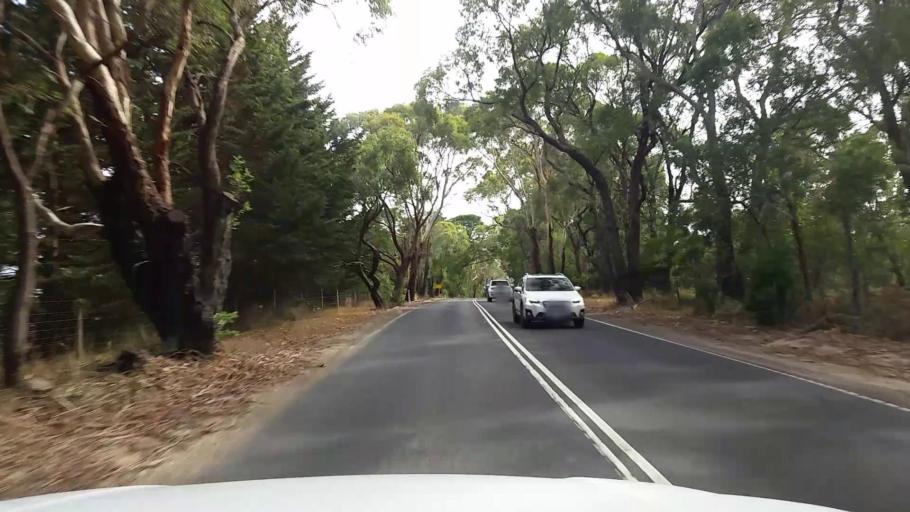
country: AU
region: Victoria
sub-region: Mornington Peninsula
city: Merricks
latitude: -38.3104
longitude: 145.0845
